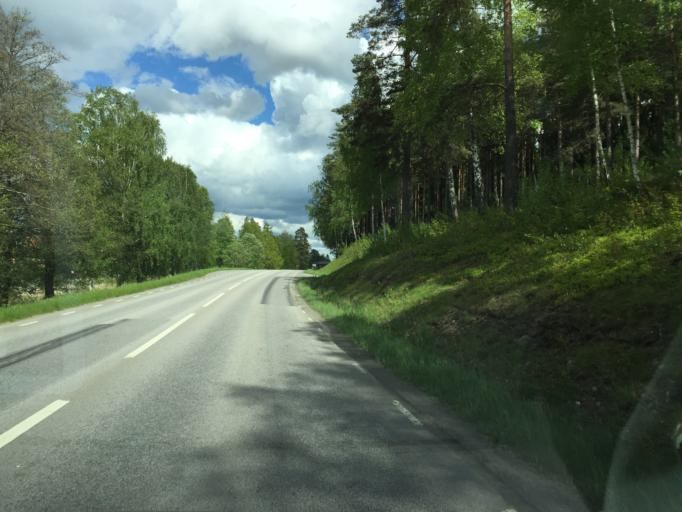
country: SE
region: OEstergoetland
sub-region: Finspangs Kommun
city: Finspang
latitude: 58.7026
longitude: 15.7609
